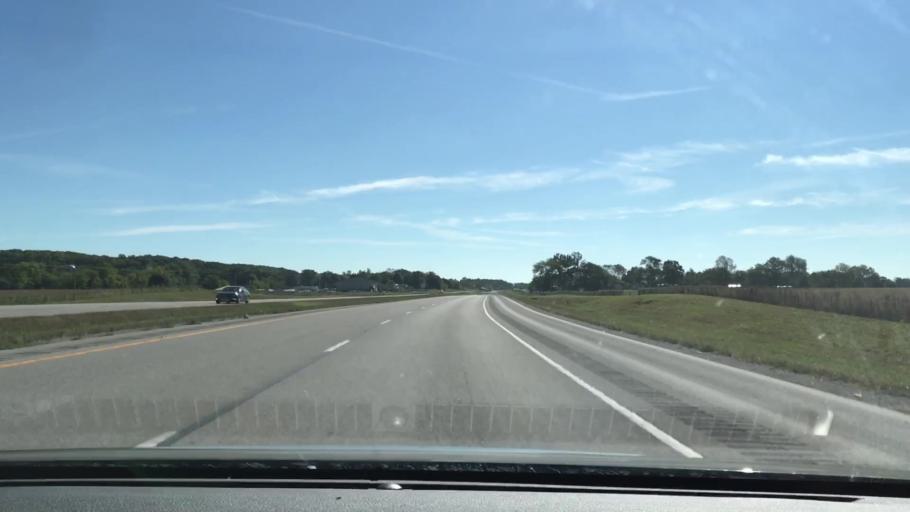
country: US
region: Kentucky
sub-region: Todd County
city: Elkton
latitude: 36.8390
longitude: -87.2433
